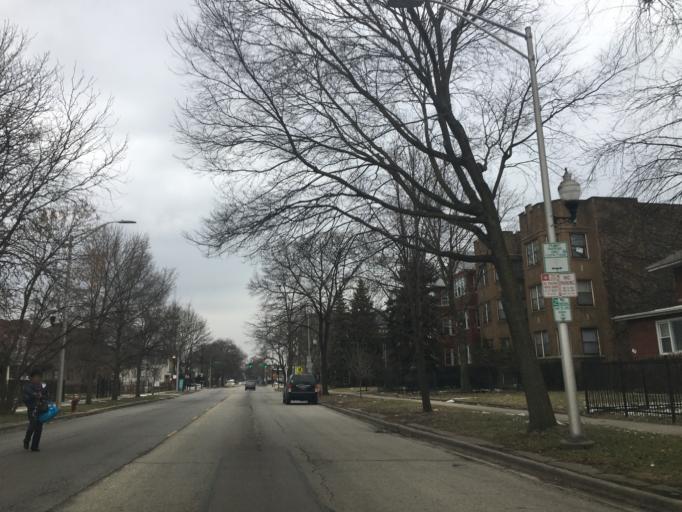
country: US
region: Illinois
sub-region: Cook County
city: Oak Park
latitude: 41.8834
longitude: -87.7748
